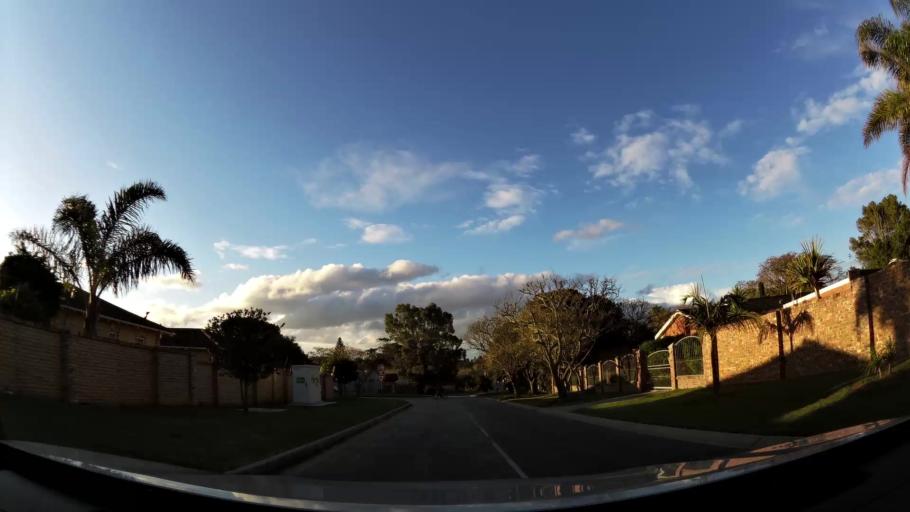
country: ZA
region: Eastern Cape
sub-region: Nelson Mandela Bay Metropolitan Municipality
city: Port Elizabeth
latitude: -33.9672
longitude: 25.4897
